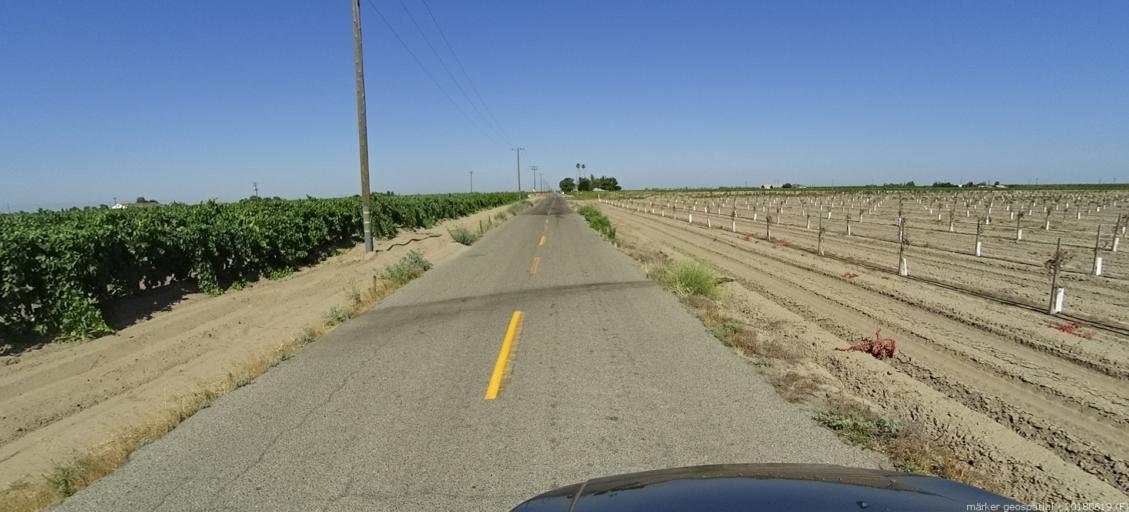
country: US
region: California
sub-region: Fresno County
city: Biola
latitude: 36.8368
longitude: -120.0041
